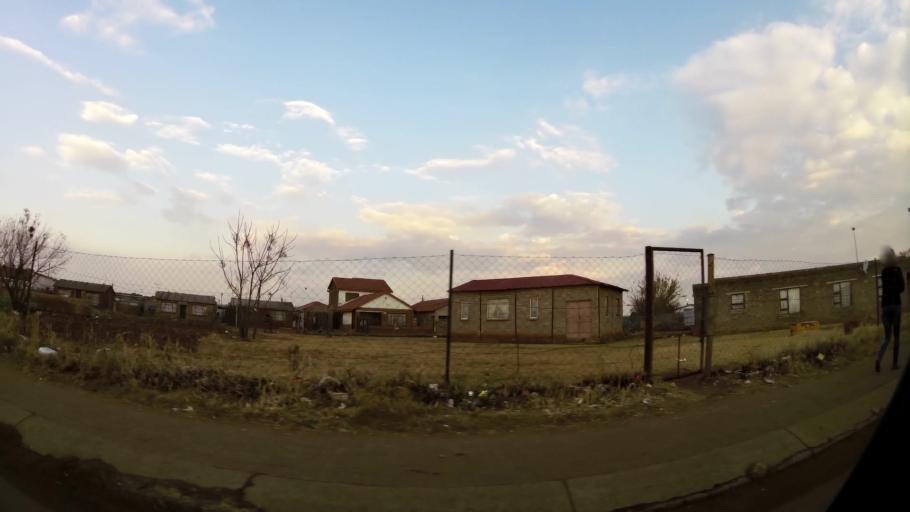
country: ZA
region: Gauteng
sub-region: City of Johannesburg Metropolitan Municipality
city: Orange Farm
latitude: -26.5620
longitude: 27.8374
